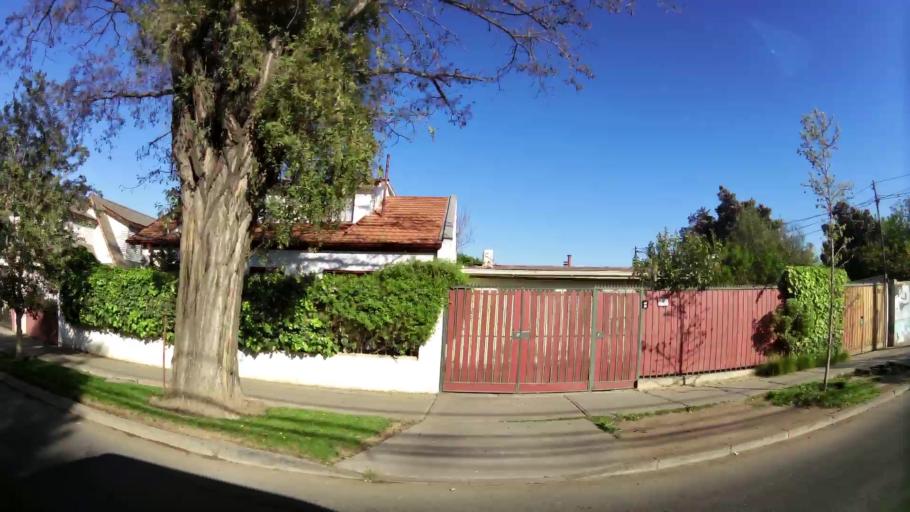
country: CL
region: Santiago Metropolitan
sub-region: Provincia de Santiago
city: Villa Presidente Frei, Nunoa, Santiago, Chile
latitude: -33.4576
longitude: -70.5665
